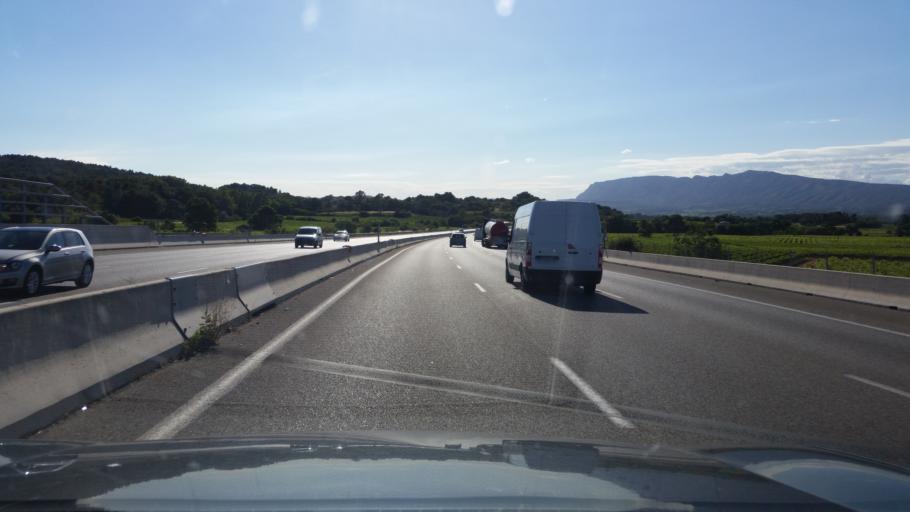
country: FR
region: Provence-Alpes-Cote d'Azur
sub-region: Departement du Var
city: Saint-Maximin-la-Sainte-Baume
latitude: 43.4718
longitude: 5.7968
